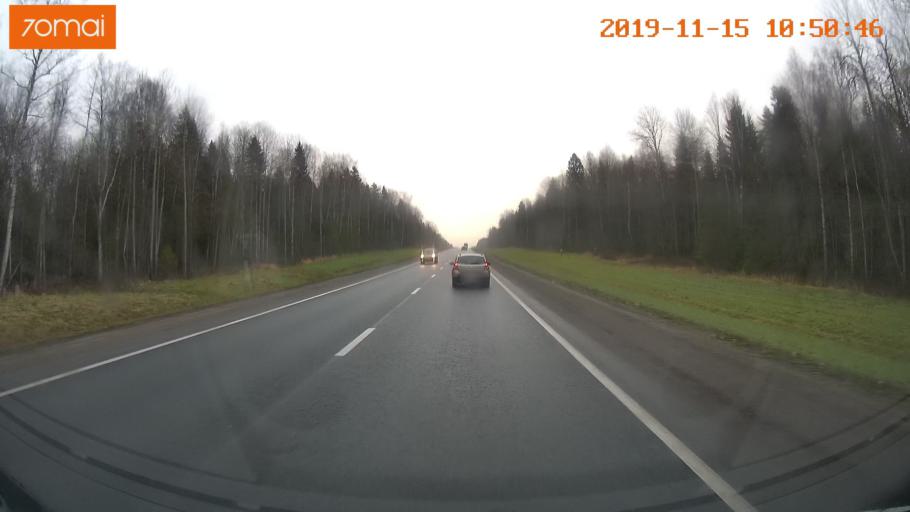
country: RU
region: Vologda
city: Chebsara
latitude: 59.1837
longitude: 38.6889
